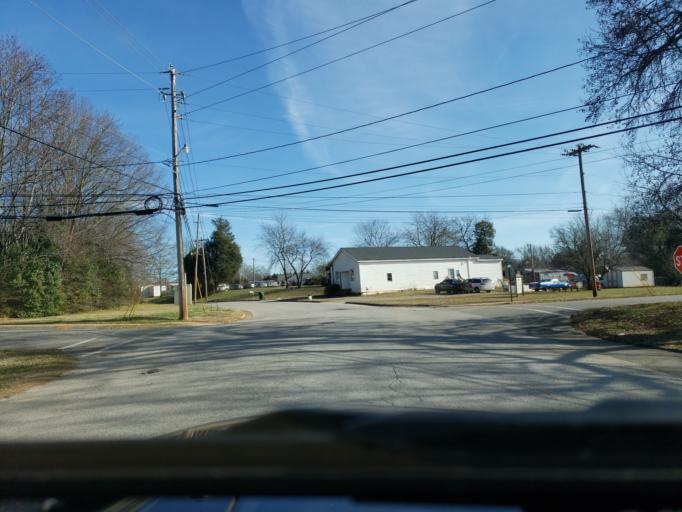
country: US
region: North Carolina
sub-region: Cleveland County
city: Kings Mountain
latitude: 35.2509
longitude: -81.3310
